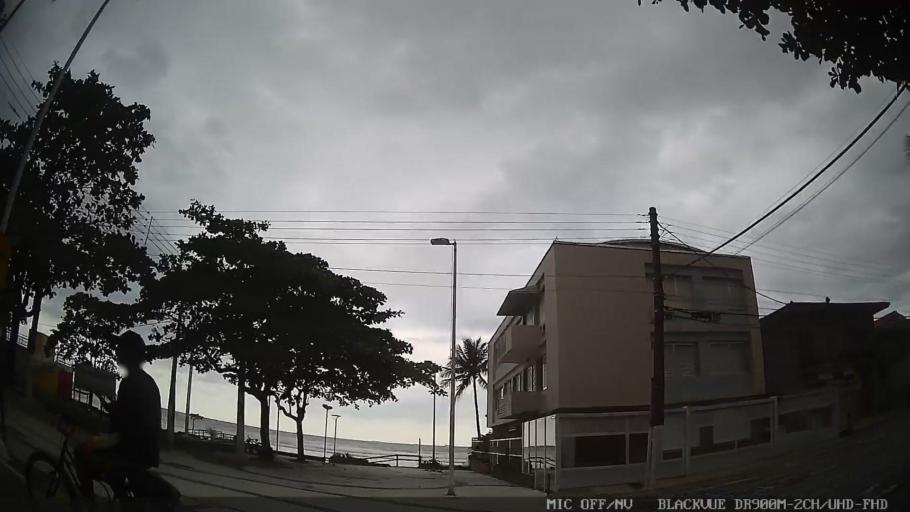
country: BR
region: Sao Paulo
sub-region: Guaruja
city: Guaruja
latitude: -23.9958
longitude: -46.2543
